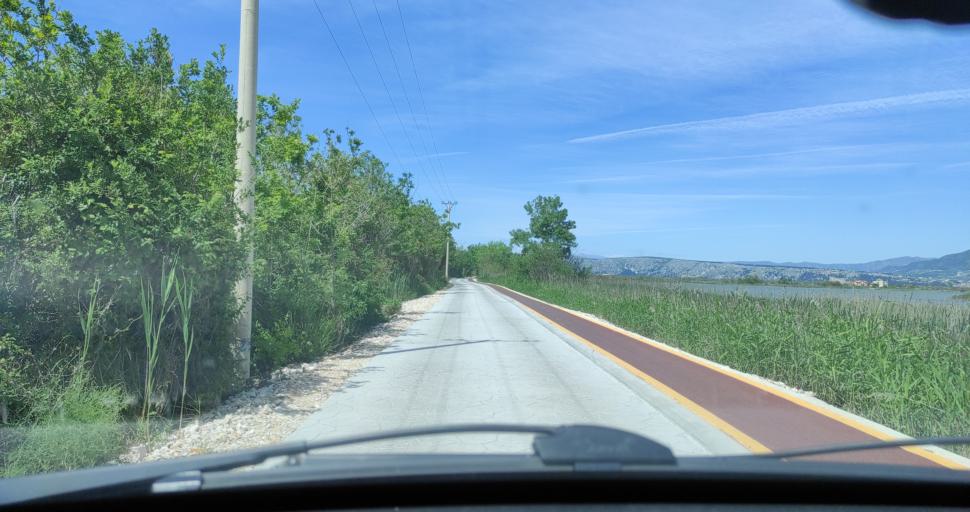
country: AL
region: Lezhe
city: Shengjin
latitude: 41.7418
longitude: 19.5820
